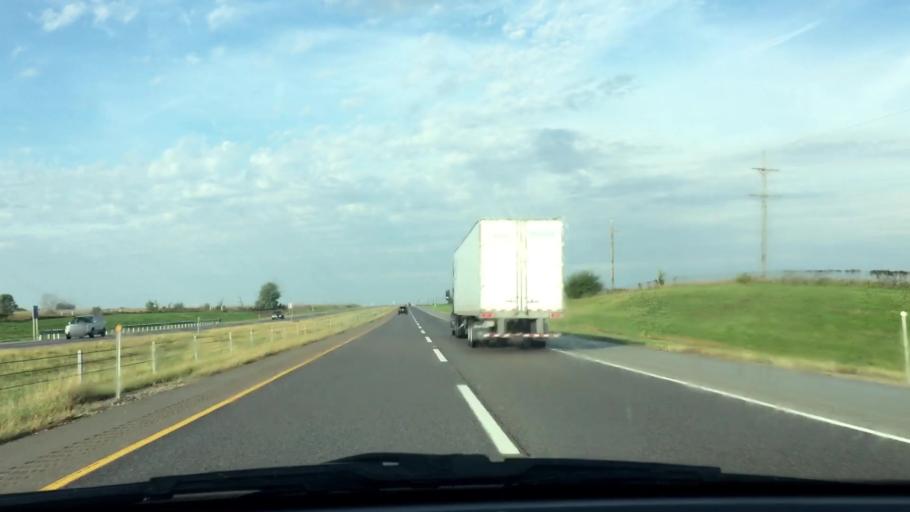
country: US
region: Illinois
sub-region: Lee County
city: Franklin Grove
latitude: 41.8229
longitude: -89.3633
